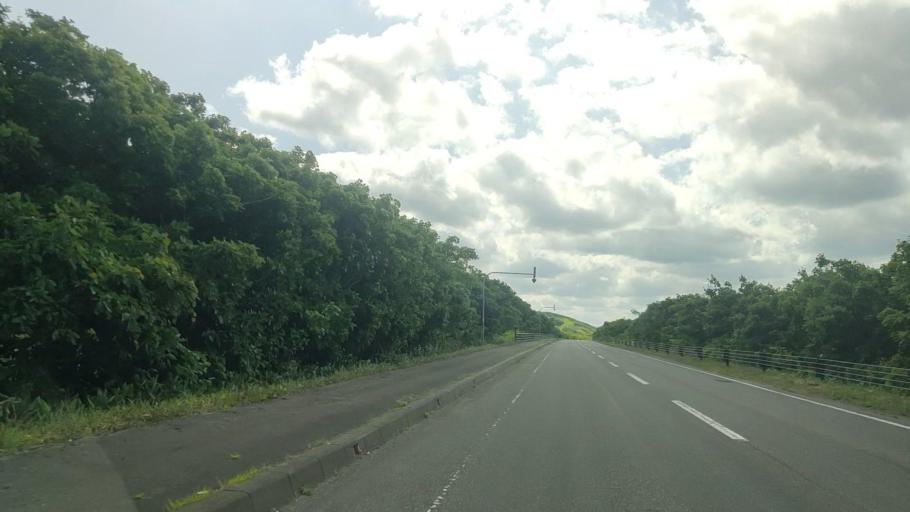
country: JP
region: Hokkaido
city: Wakkanai
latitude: 45.3645
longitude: 141.6620
